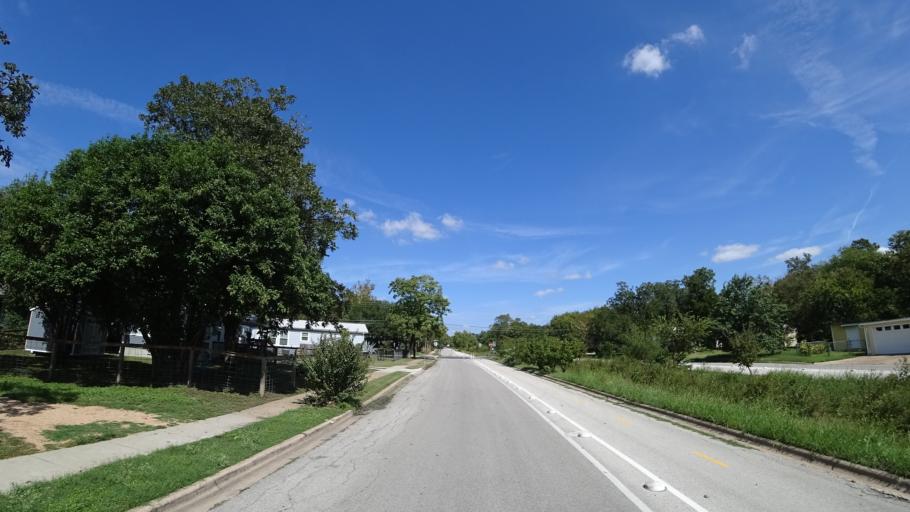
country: US
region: Texas
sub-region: Travis County
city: Austin
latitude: 30.3411
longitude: -97.7289
